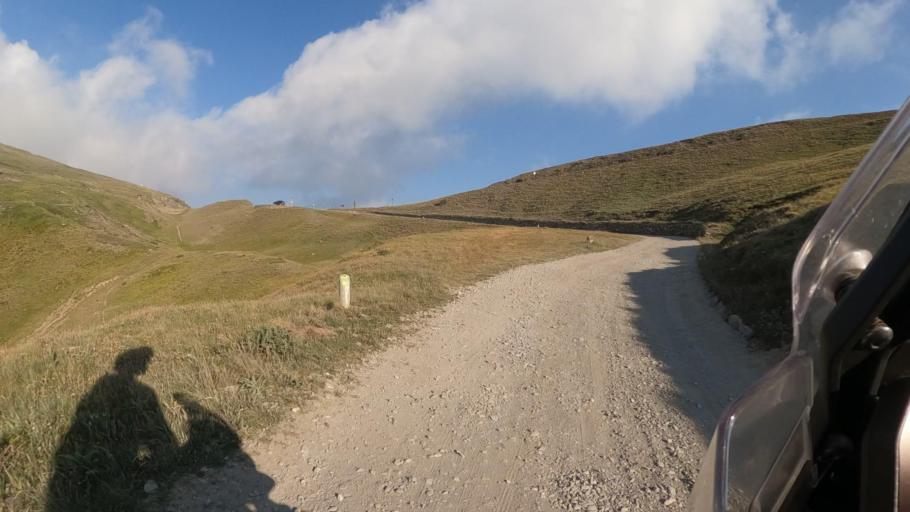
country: IT
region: Piedmont
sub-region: Provincia di Torino
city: Exilles
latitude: 45.0701
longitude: 6.9591
